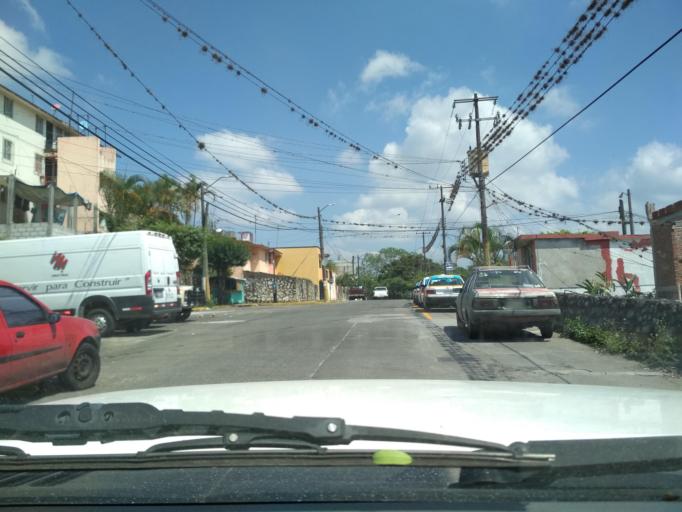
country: MX
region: Veracruz
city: Cordoba
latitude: 18.8783
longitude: -96.9134
